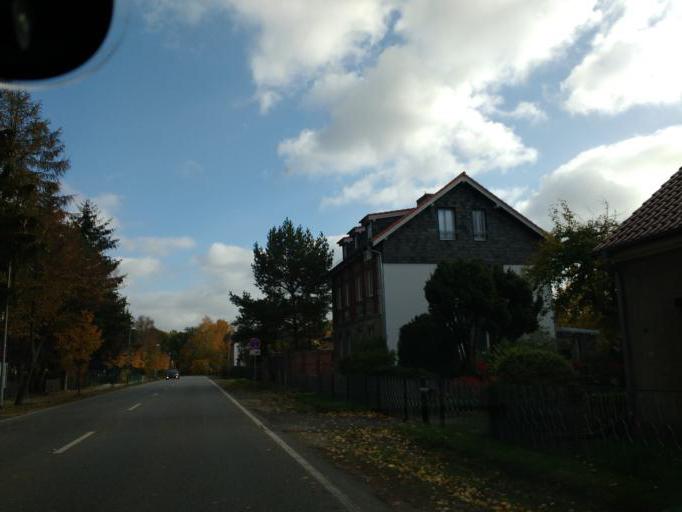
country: DE
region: Brandenburg
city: Petershagen
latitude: 52.5595
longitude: 13.7725
